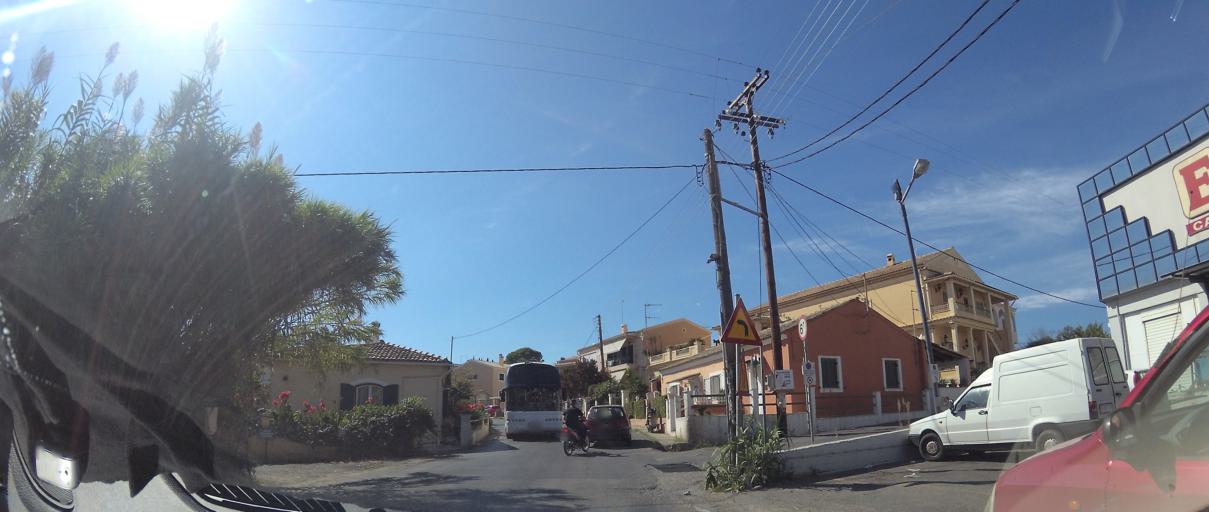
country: GR
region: Ionian Islands
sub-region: Nomos Kerkyras
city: Alepou
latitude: 39.6135
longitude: 19.8876
